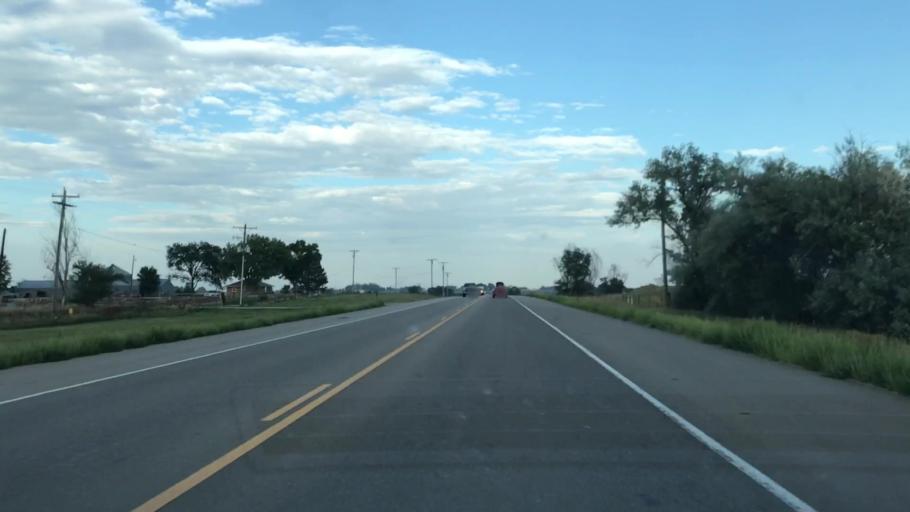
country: US
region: Colorado
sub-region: Weld County
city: Mead
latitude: 40.2038
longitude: -105.0275
